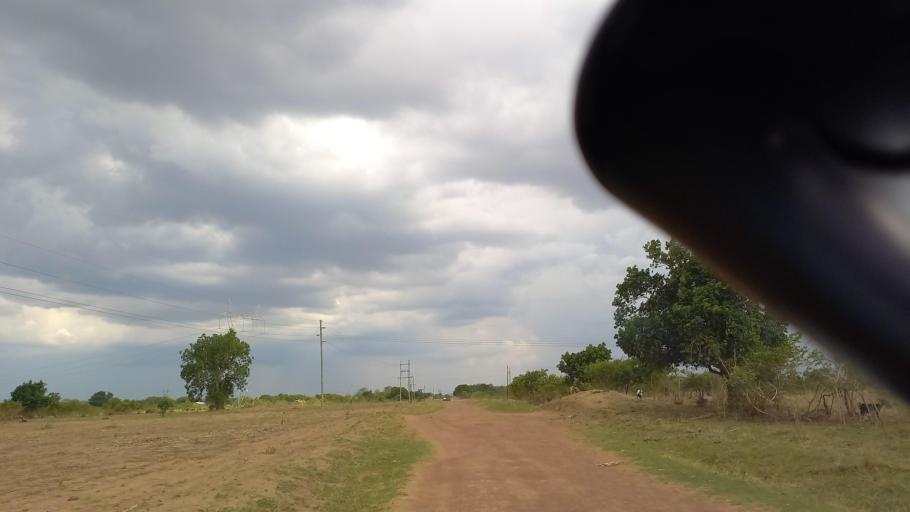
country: ZM
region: Lusaka
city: Kafue
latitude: -15.8471
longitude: 28.1024
